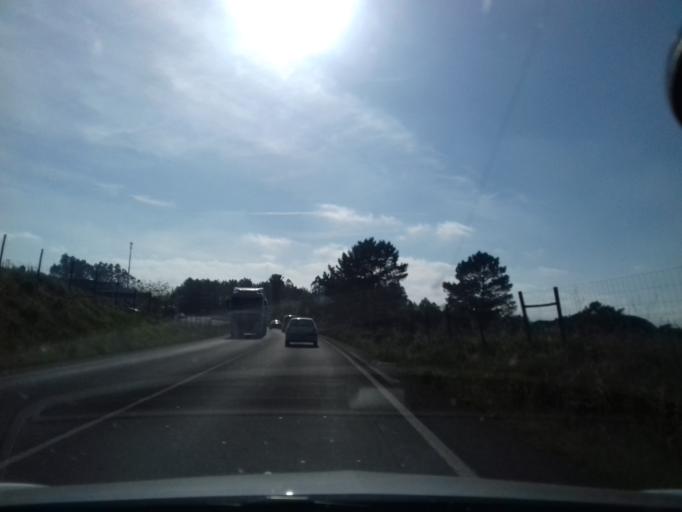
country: PT
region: Leiria
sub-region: Leiria
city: Maceira
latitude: 39.7104
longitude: -8.8565
